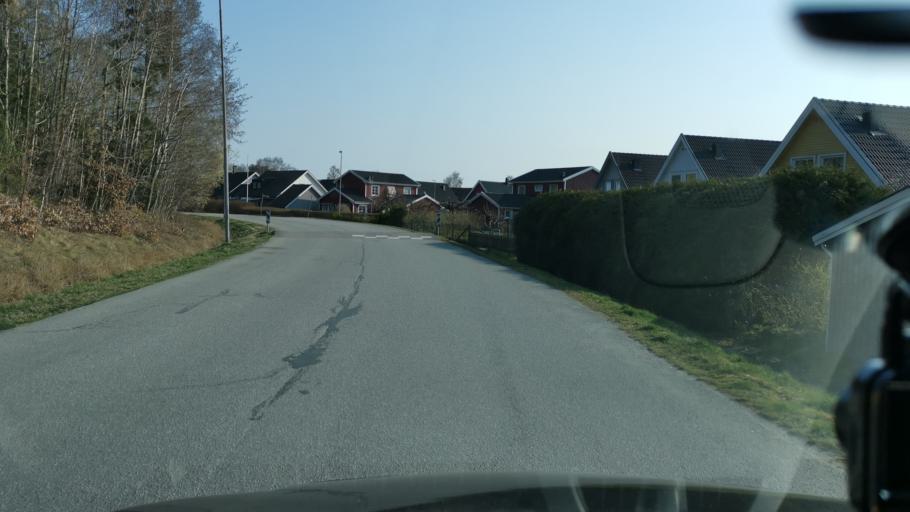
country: SE
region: Vaestra Goetaland
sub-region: Kungalvs Kommun
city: Kode
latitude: 57.9449
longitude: 11.8381
